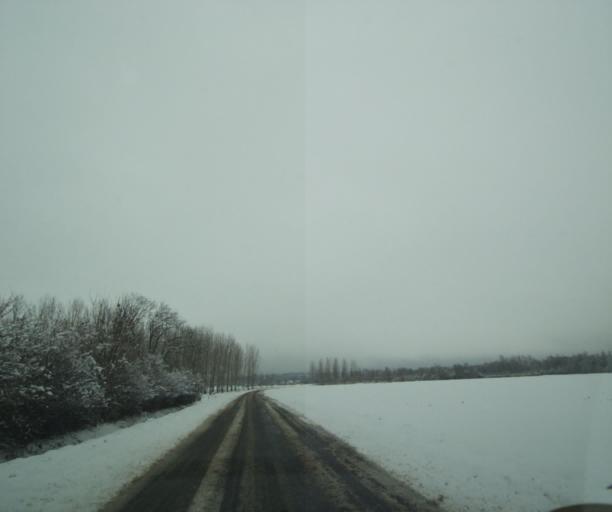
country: FR
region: Champagne-Ardenne
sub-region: Departement de la Haute-Marne
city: Saint-Dizier
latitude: 48.5738
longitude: 4.8901
